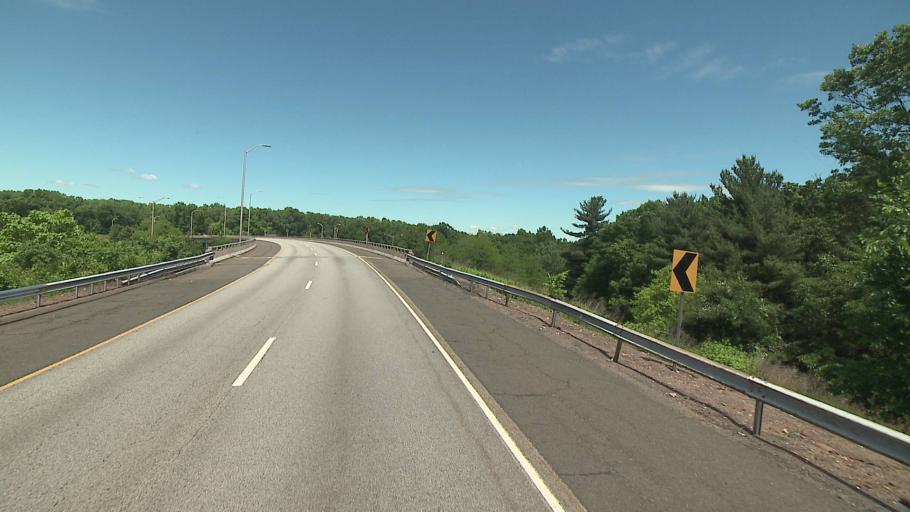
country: US
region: Connecticut
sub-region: Hartford County
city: Windsor Locks
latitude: 41.8977
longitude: -72.6387
